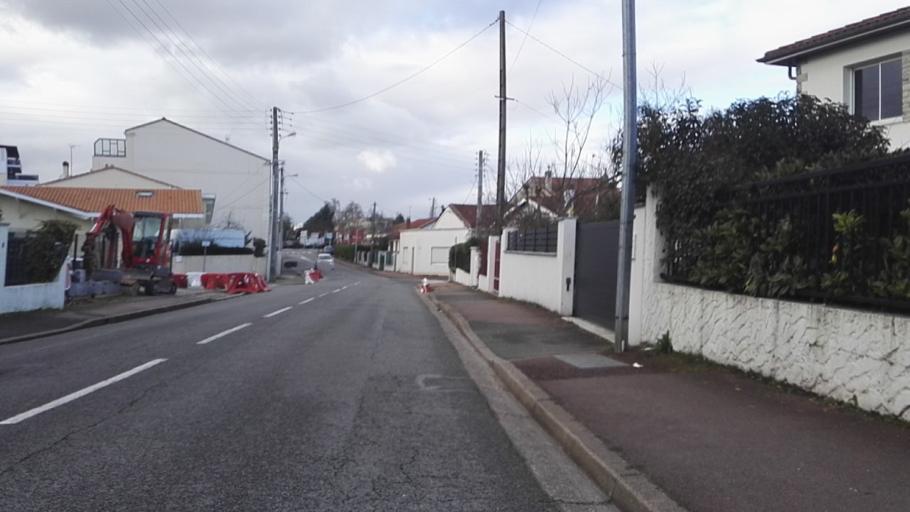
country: FR
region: Aquitaine
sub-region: Departement de la Gironde
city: Talence
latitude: 44.8058
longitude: -0.5846
